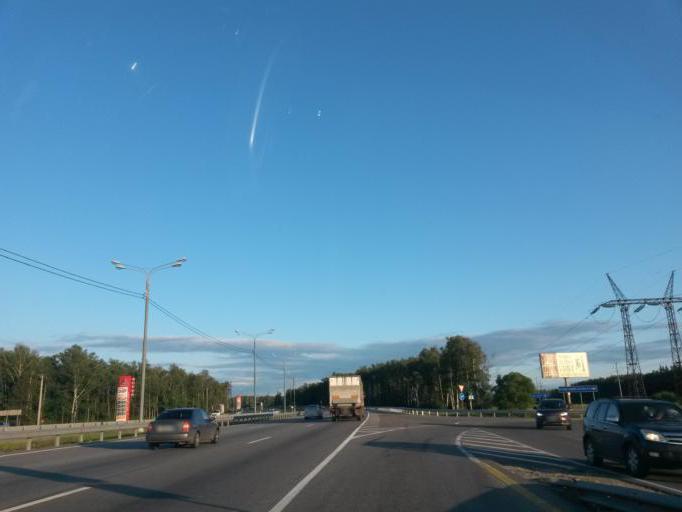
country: RU
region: Moskovskaya
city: Vostryakovo
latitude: 55.3688
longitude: 37.7825
